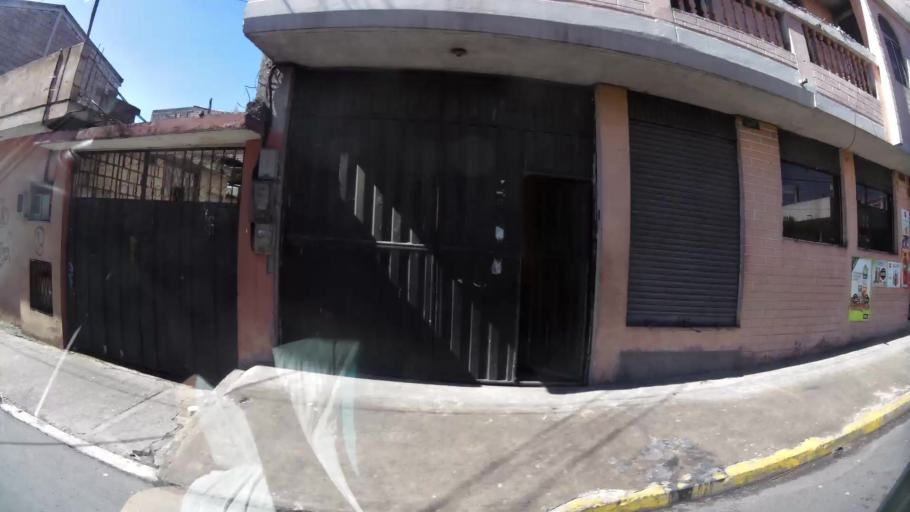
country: EC
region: Pichincha
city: Quito
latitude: -0.2859
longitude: -78.5609
